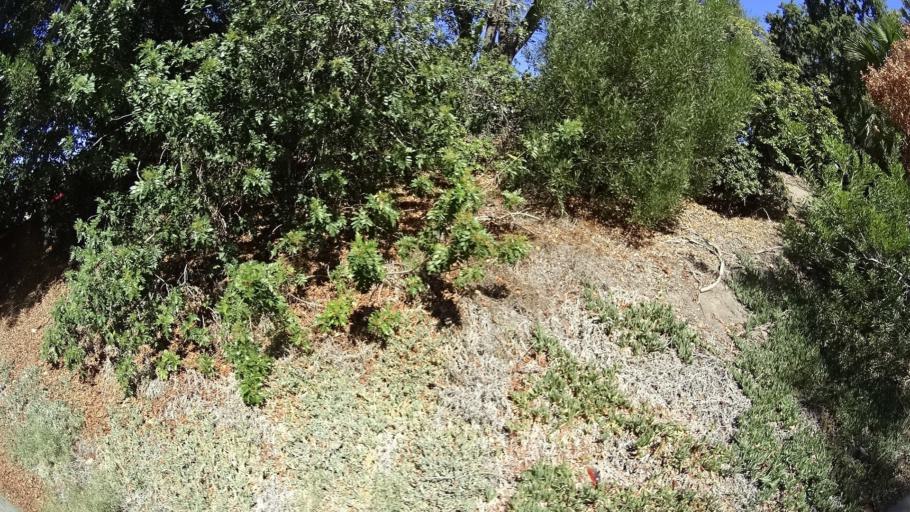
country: US
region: California
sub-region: San Diego County
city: Bonita
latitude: 32.6583
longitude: -117.0172
